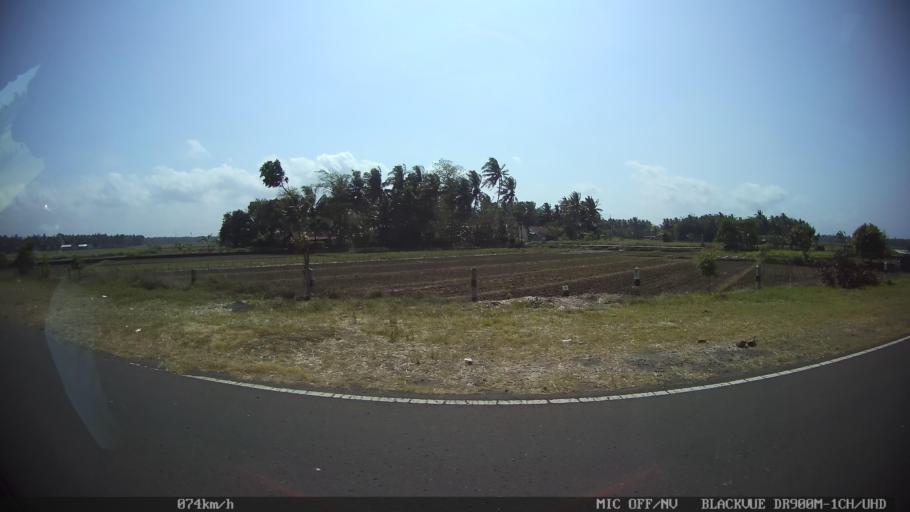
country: ID
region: Daerah Istimewa Yogyakarta
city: Srandakan
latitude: -7.9629
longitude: 110.2042
